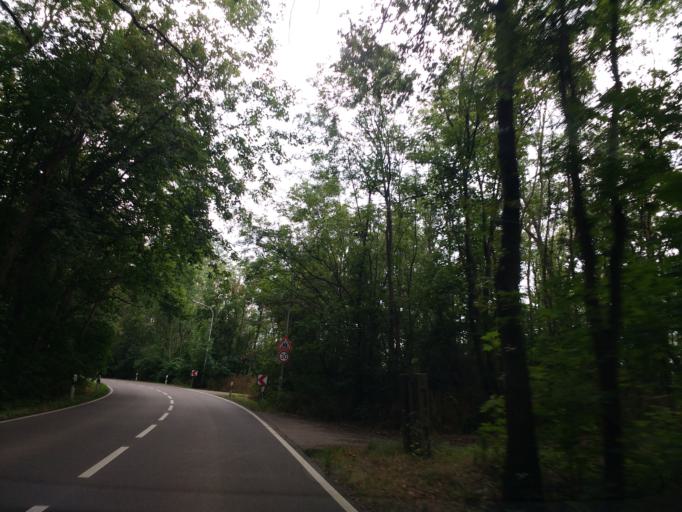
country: DE
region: Saxony-Anhalt
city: Dieskau
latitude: 51.4273
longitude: 12.0272
